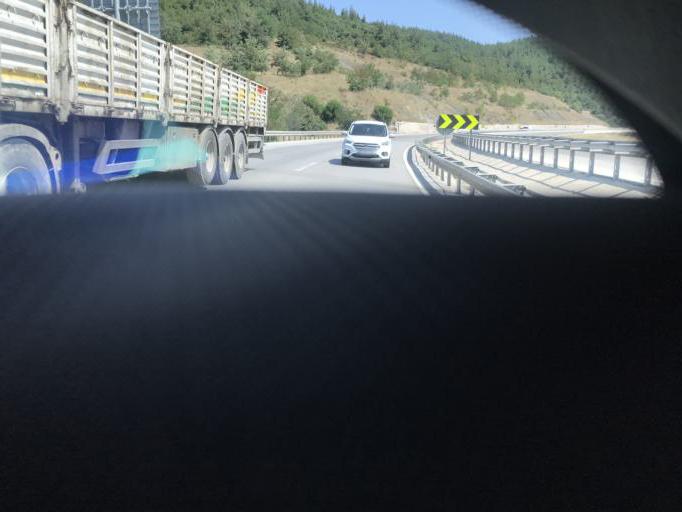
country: TR
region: Balikesir
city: Golcuk
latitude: 39.3529
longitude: 27.9478
